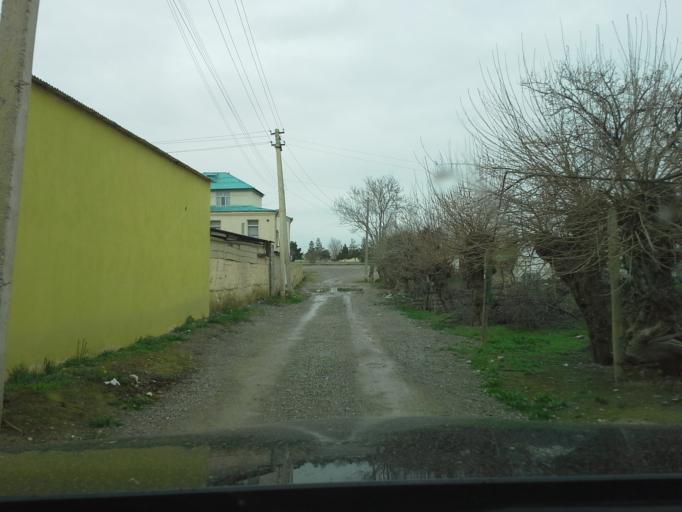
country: TM
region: Ahal
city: Abadan
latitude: 37.9641
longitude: 58.2239
